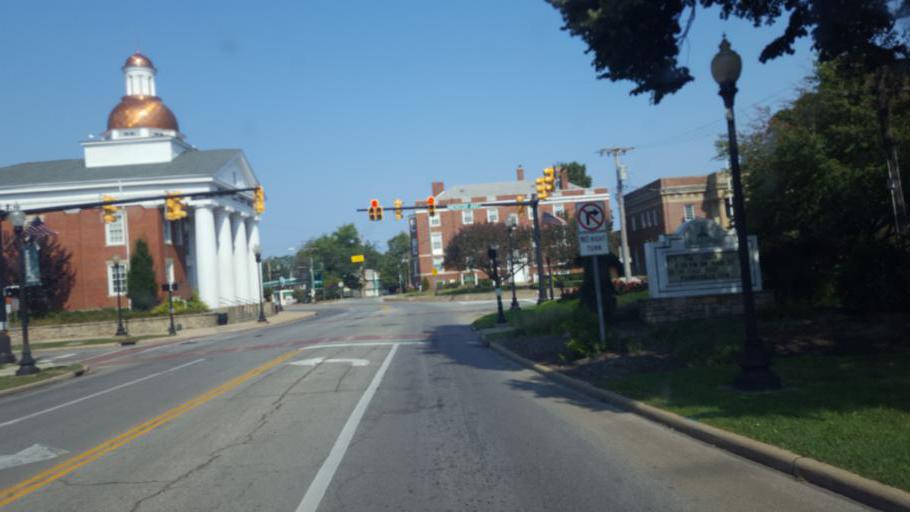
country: US
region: Ohio
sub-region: Lake County
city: Painesville
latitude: 41.7239
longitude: -81.2449
